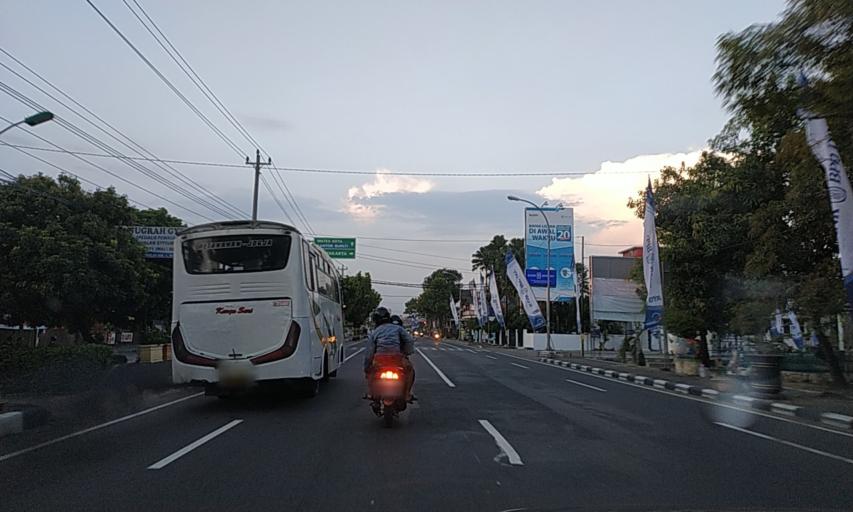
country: ID
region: Daerah Istimewa Yogyakarta
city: Srandakan
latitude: -7.8664
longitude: 110.1501
